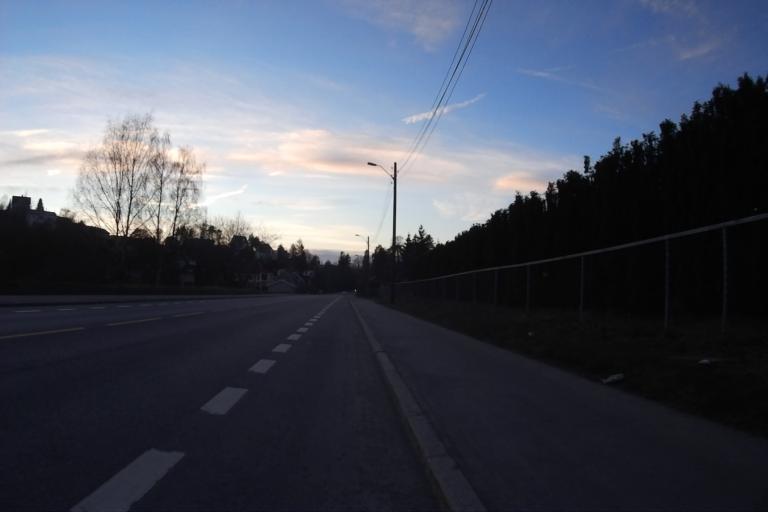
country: NO
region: Oslo
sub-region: Oslo
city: Oslo
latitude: 59.8991
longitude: 10.8297
